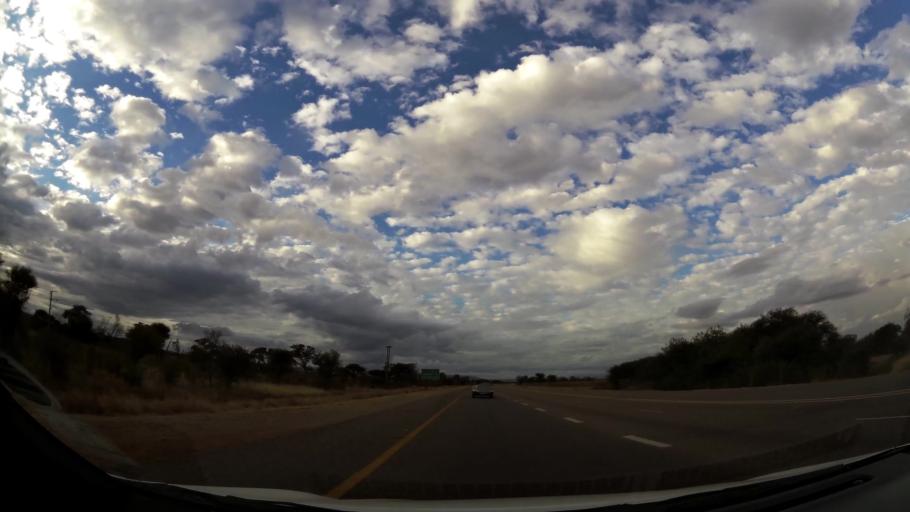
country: ZA
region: Limpopo
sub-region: Waterberg District Municipality
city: Modimolle
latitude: -24.5007
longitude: 28.7355
